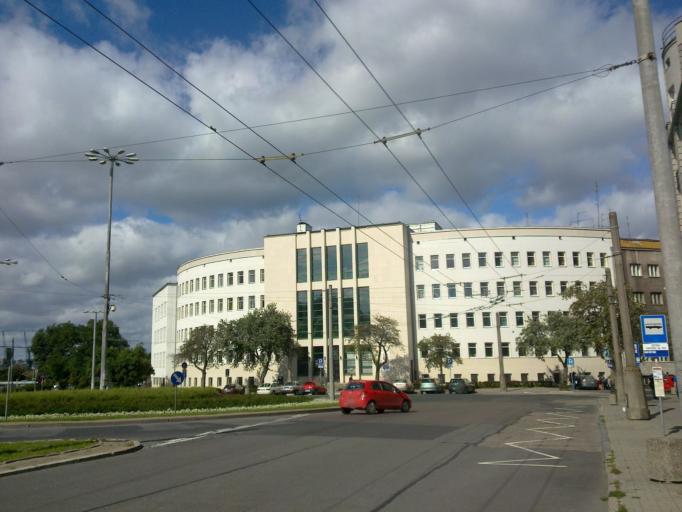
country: PL
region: Pomeranian Voivodeship
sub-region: Gdynia
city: Gdynia
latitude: 54.5214
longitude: 18.5310
